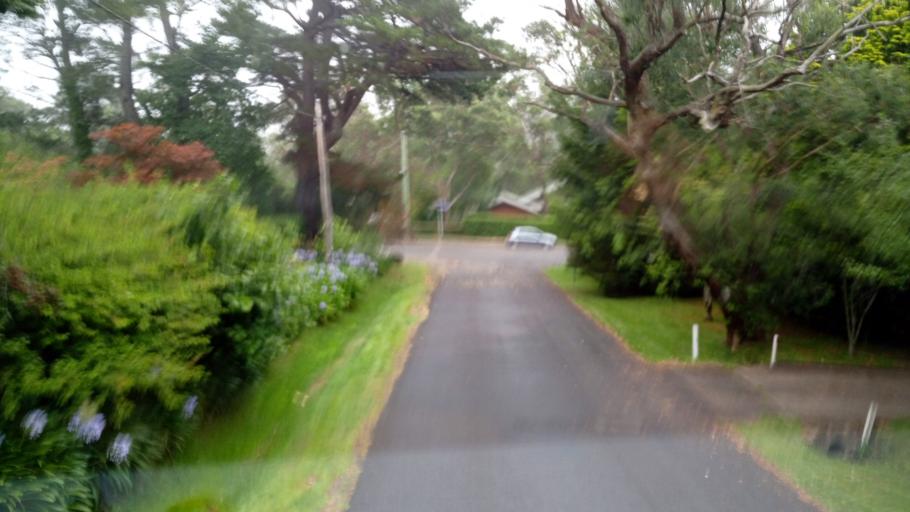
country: AU
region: New South Wales
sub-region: Blue Mountains Municipality
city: Leura
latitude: -33.7207
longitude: 150.3393
